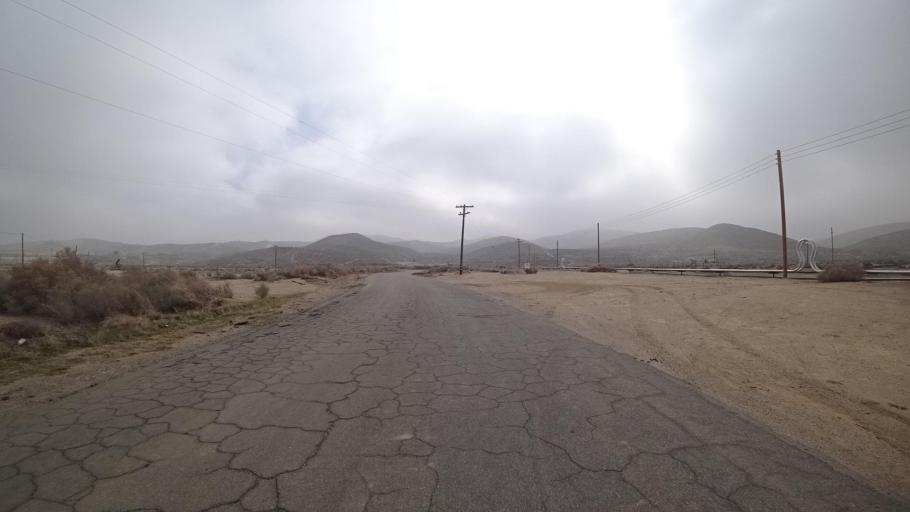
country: US
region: California
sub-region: Kern County
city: Maricopa
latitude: 35.0412
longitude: -119.3846
